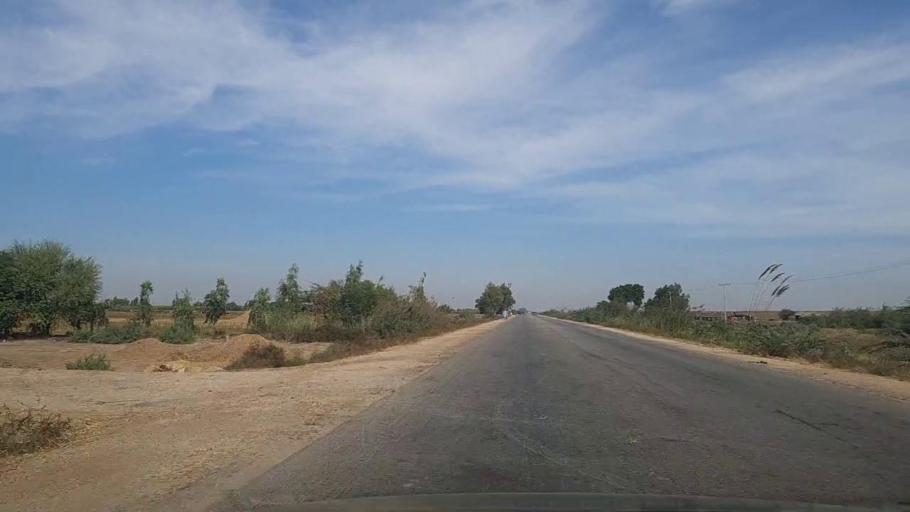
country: PK
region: Sindh
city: Daro Mehar
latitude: 24.9390
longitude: 68.1085
